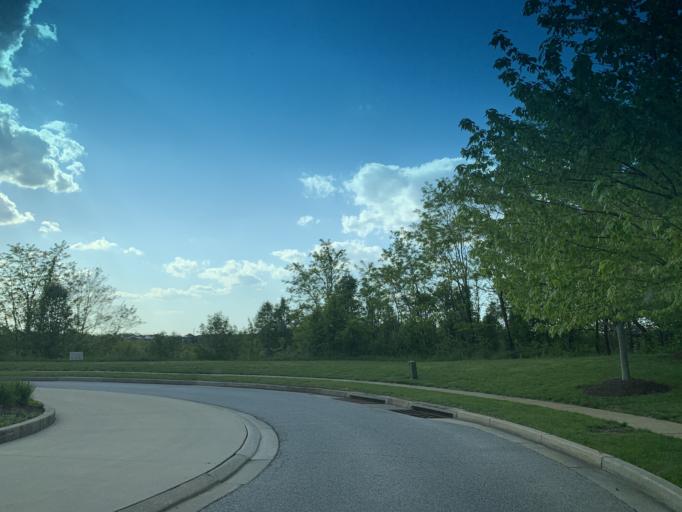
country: US
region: Maryland
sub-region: Baltimore County
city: White Marsh
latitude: 39.4031
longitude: -76.4368
